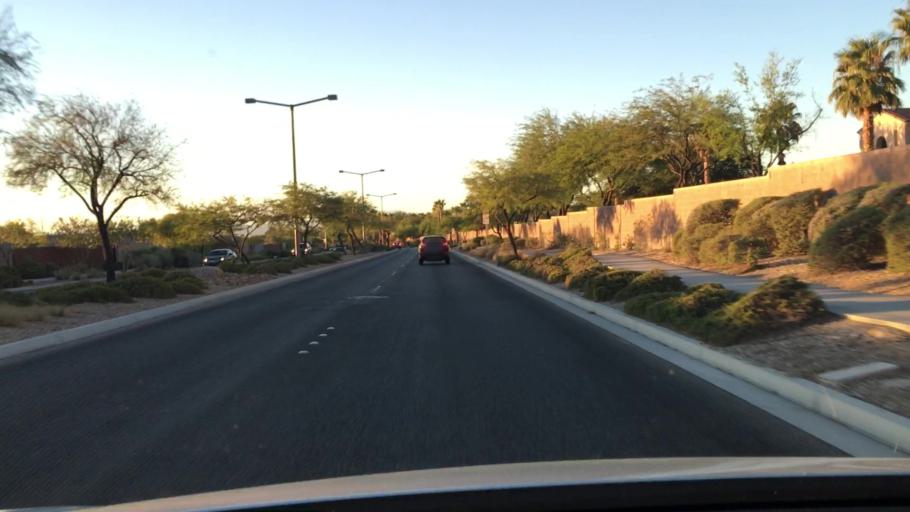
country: US
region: Nevada
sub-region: Clark County
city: Summerlin South
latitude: 36.1488
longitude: -115.3425
